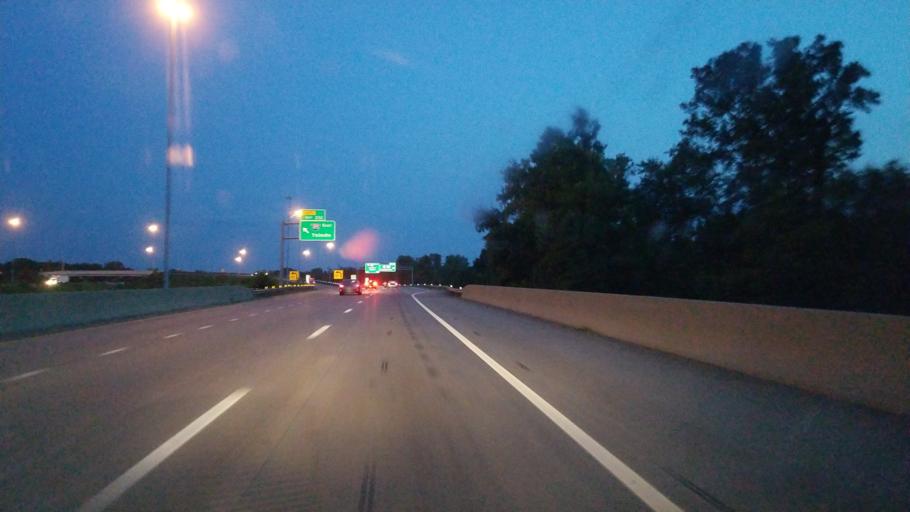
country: US
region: Ohio
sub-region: Lucas County
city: Sylvania
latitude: 41.6906
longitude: -83.6964
